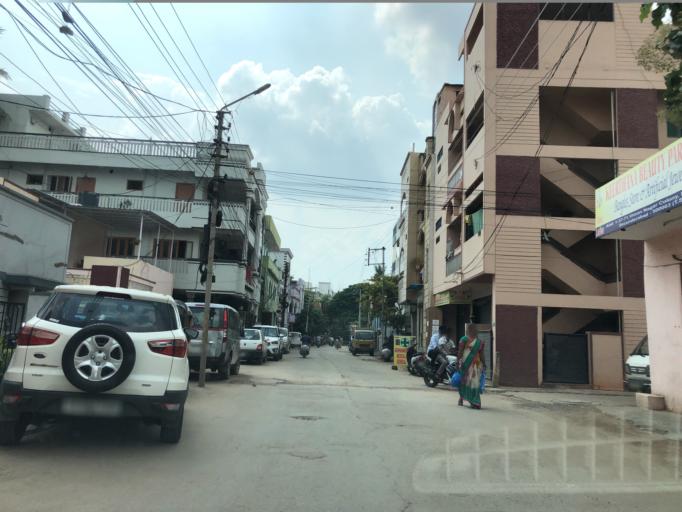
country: IN
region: Telangana
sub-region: Hyderabad
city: Malkajgiri
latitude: 17.4464
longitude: 78.4832
